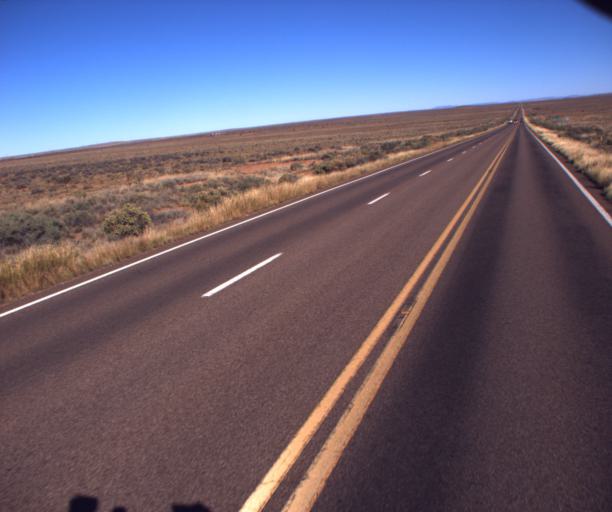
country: US
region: Arizona
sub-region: Navajo County
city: Snowflake
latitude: 34.6962
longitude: -110.1075
